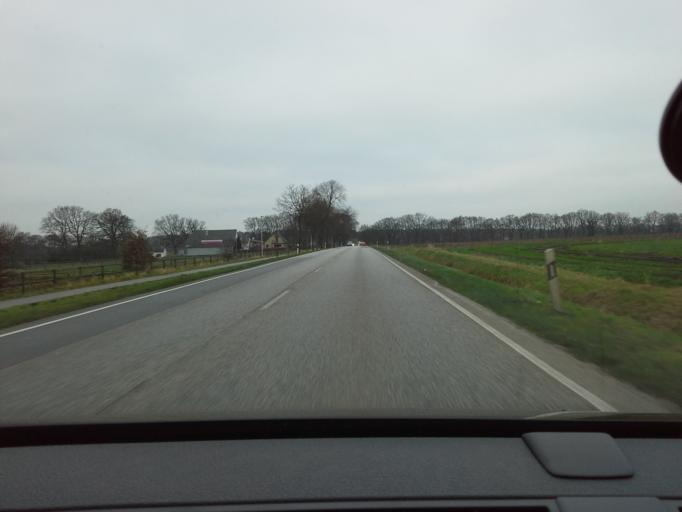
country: DE
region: Schleswig-Holstein
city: Quickborn
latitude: 53.7400
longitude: 9.8904
